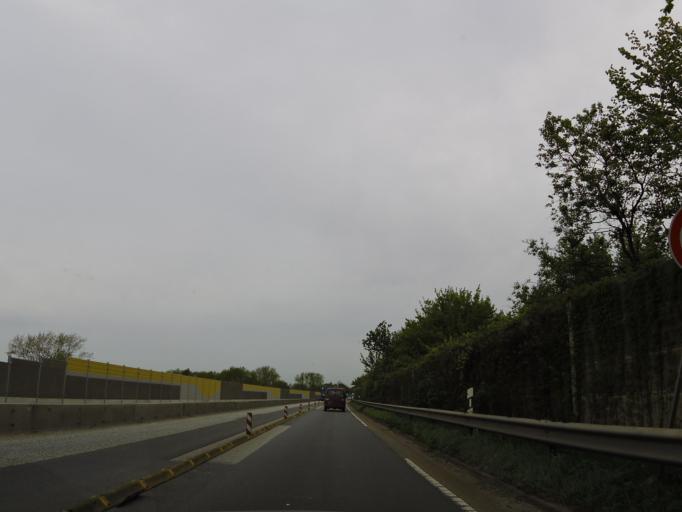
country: DE
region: Schleswig-Holstein
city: Kremperheide
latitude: 53.9065
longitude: 9.4902
